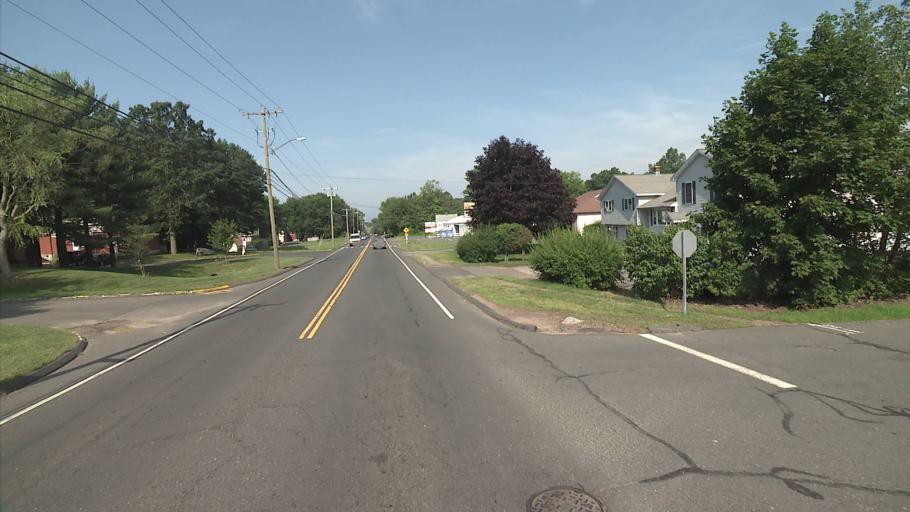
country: US
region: Connecticut
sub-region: New Haven County
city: Wolcott
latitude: 41.5551
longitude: -72.9585
